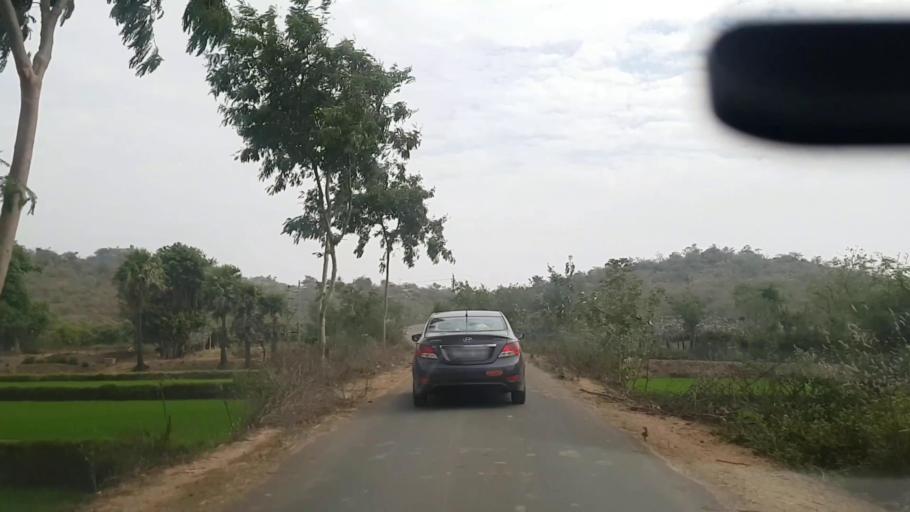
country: IN
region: Telangana
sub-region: Rangareddi
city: Lal Bahadur Nagar
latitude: 17.1761
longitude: 78.7763
